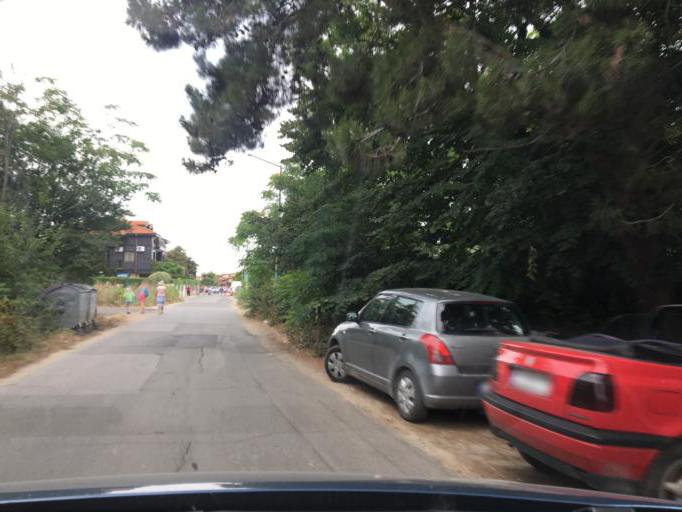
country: BG
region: Burgas
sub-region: Obshtina Sozopol
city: Sozopol
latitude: 42.4062
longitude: 27.7114
